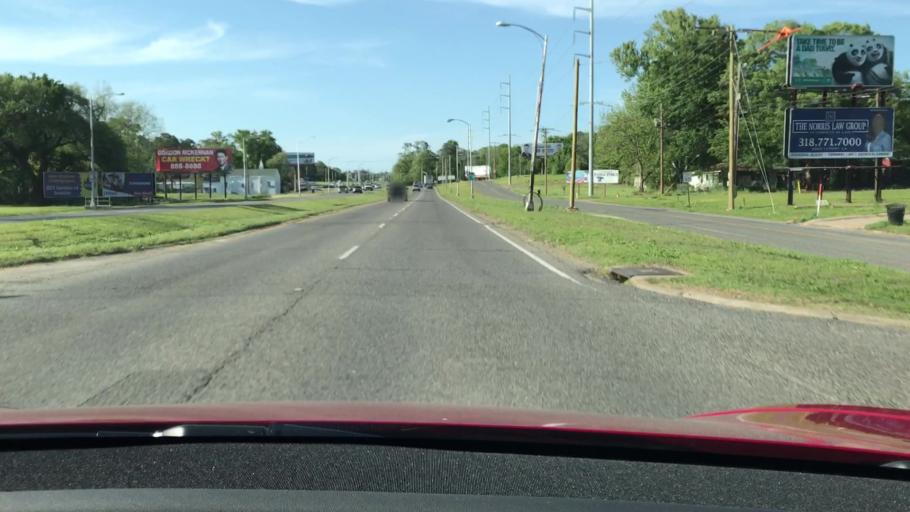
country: US
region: Louisiana
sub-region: Bossier Parish
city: Bossier City
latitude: 32.4891
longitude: -93.7242
